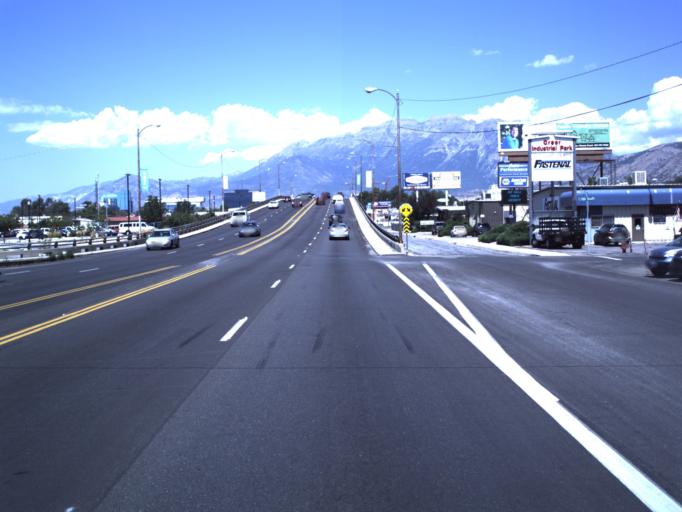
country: US
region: Utah
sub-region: Utah County
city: Provo
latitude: 40.2229
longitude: -111.6587
